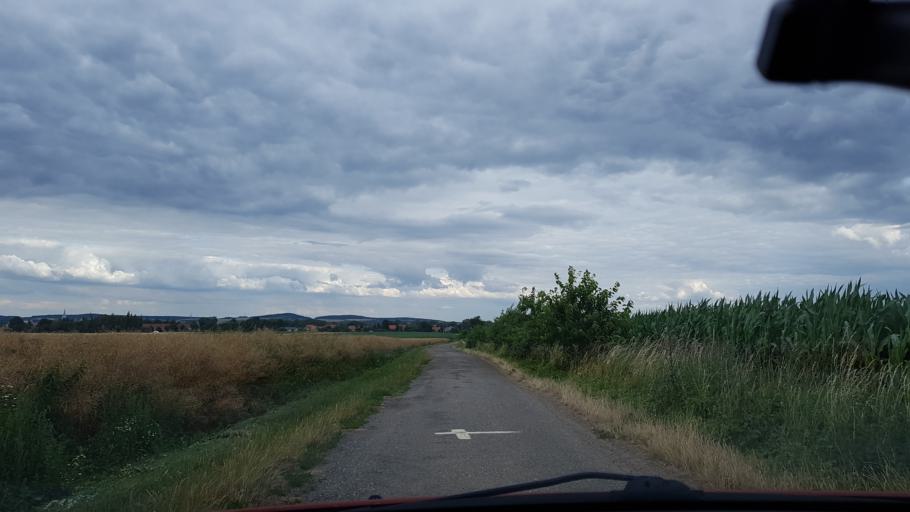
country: PL
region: Lower Silesian Voivodeship
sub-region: Powiat zabkowicki
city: Zabkowice Slaskie
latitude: 50.5707
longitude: 16.7732
